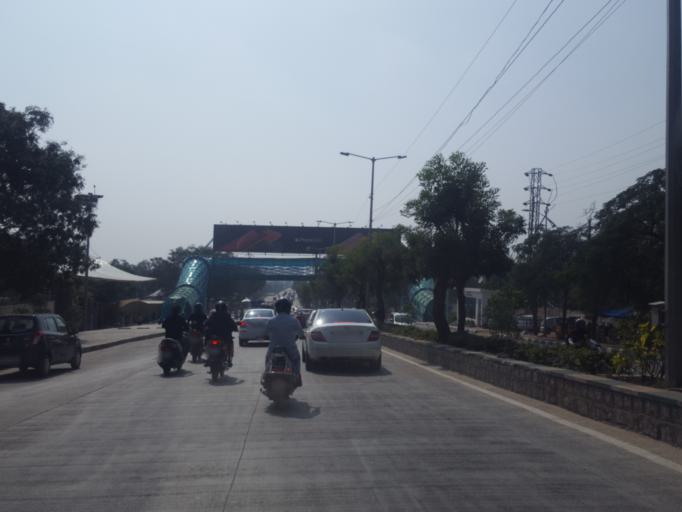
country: IN
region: Telangana
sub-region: Medak
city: Serilingampalle
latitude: 17.4373
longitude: 78.3478
